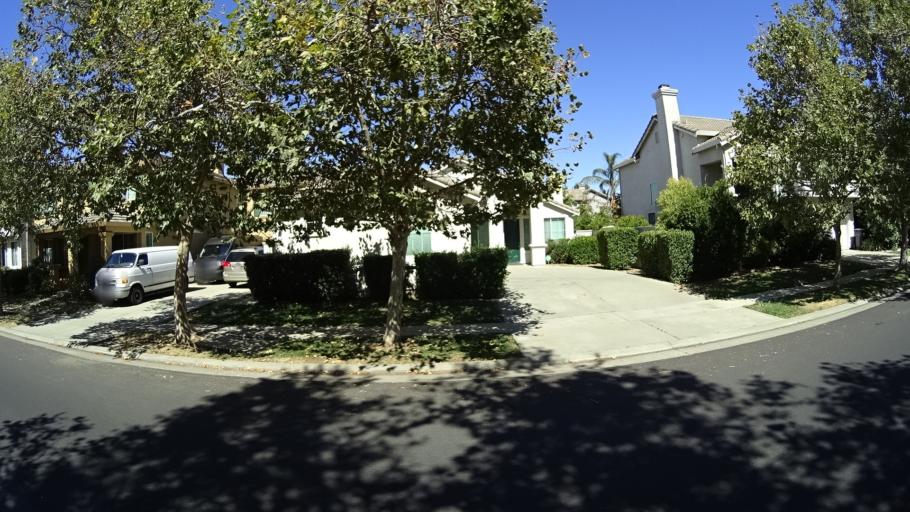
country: US
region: California
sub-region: Sacramento County
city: Laguna
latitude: 38.4172
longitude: -121.4733
